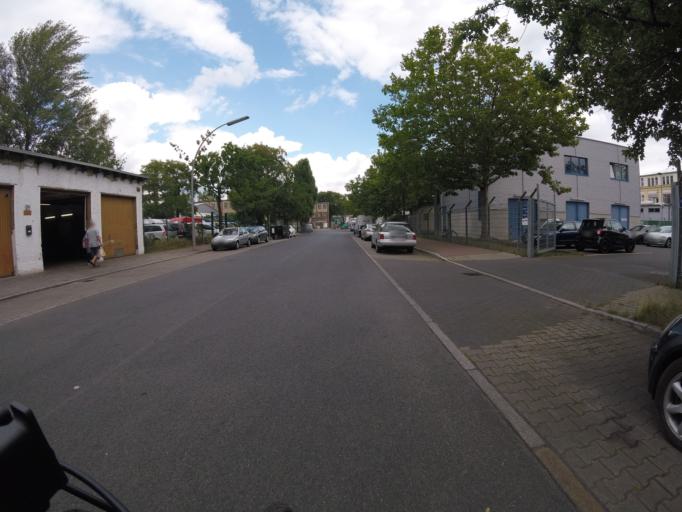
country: DE
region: Berlin
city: Haselhorst
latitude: 52.5401
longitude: 13.2227
